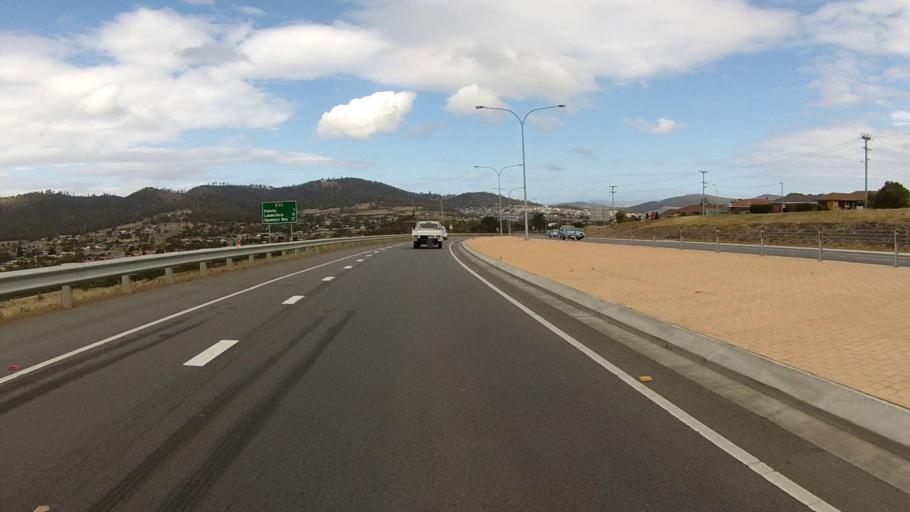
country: AU
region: Tasmania
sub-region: Clarence
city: Rokeby
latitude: -42.8891
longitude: 147.4312
